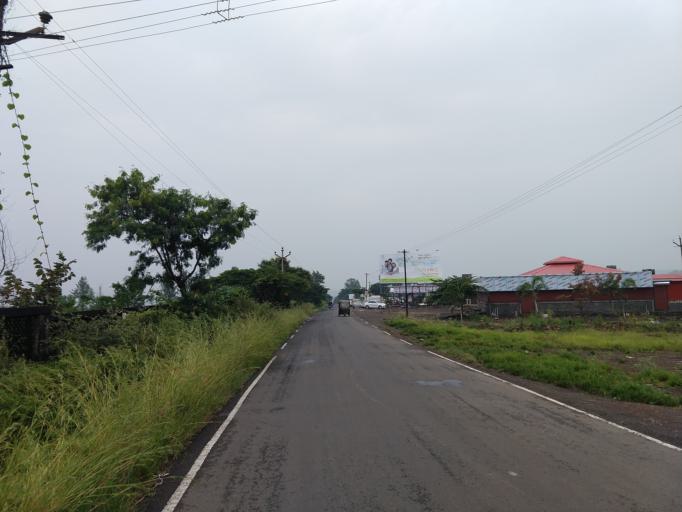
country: IN
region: Maharashtra
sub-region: Pune Division
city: Khed
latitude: 18.4033
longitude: 73.9115
